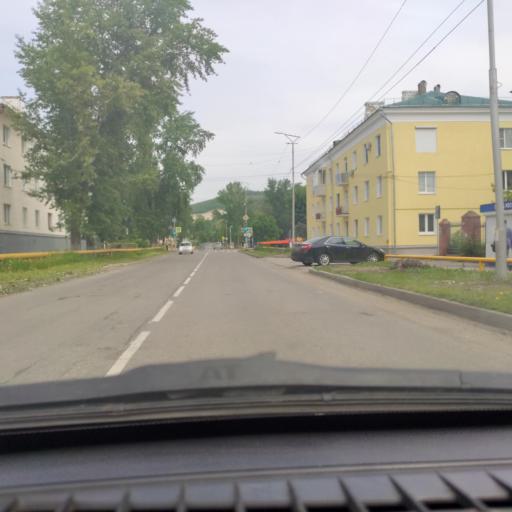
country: RU
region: Samara
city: Zhigulevsk
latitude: 53.4003
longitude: 49.4977
